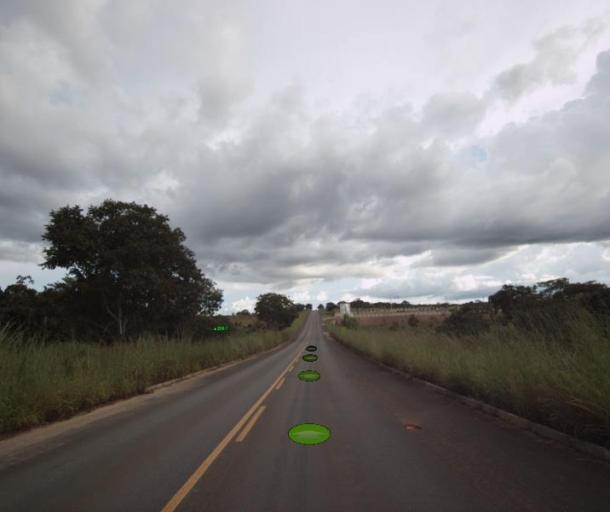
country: BR
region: Goias
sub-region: Niquelandia
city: Niquelandia
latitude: -14.4881
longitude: -48.4890
